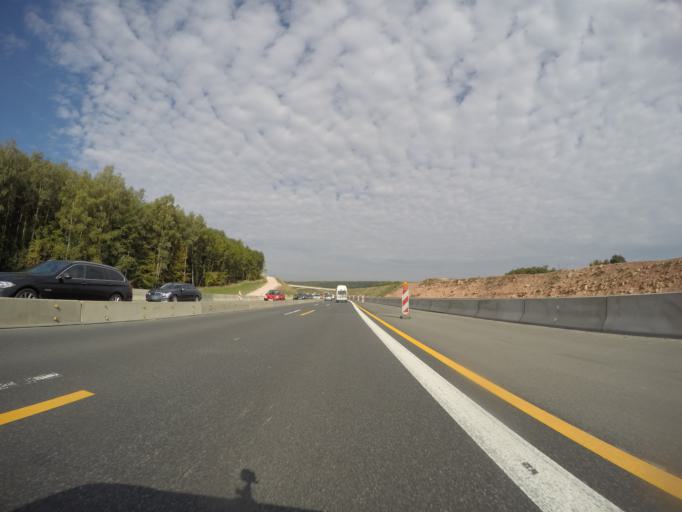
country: DE
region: Bavaria
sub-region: Regierungsbezirk Unterfranken
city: Weibersbrunn
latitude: 49.9288
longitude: 9.3534
